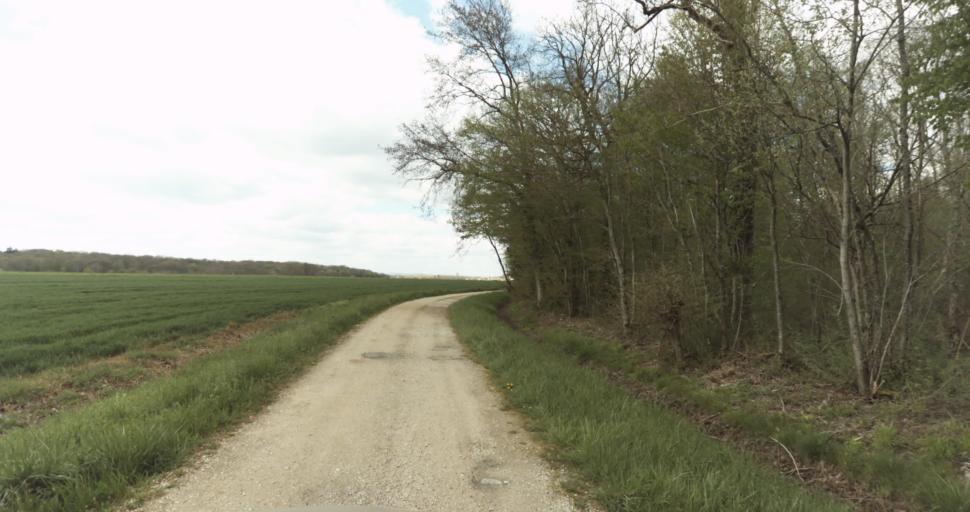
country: FR
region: Franche-Comte
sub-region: Departement du Jura
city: Champvans
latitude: 47.1504
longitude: 5.4214
